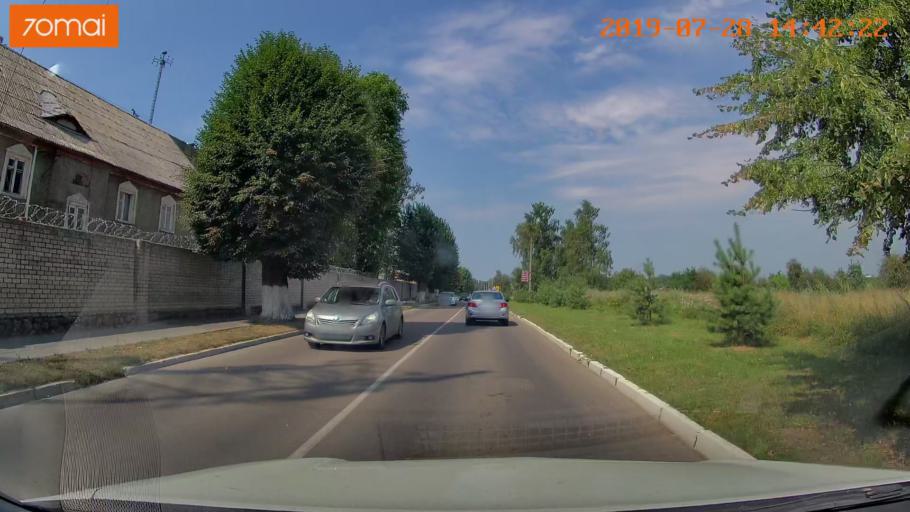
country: RU
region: Kaliningrad
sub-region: Gorod Kaliningrad
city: Yantarnyy
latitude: 54.8595
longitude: 19.9424
